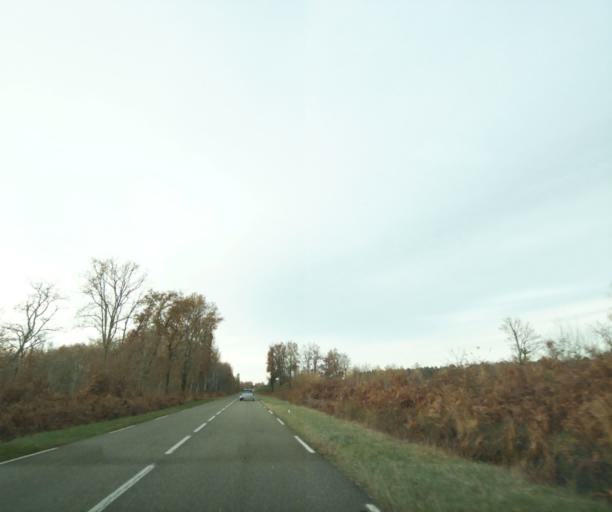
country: FR
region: Aquitaine
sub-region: Departement de la Gironde
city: Bazas
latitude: 44.2730
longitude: -0.2439
